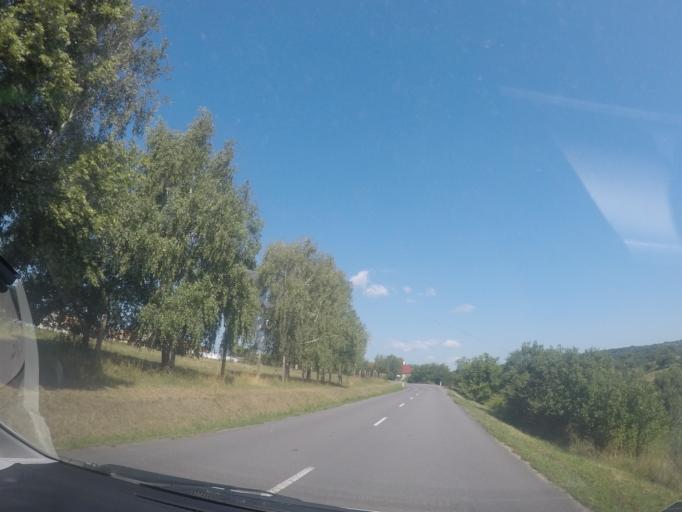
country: SK
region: Banskobystricky
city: Dudince
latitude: 48.2013
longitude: 18.8077
